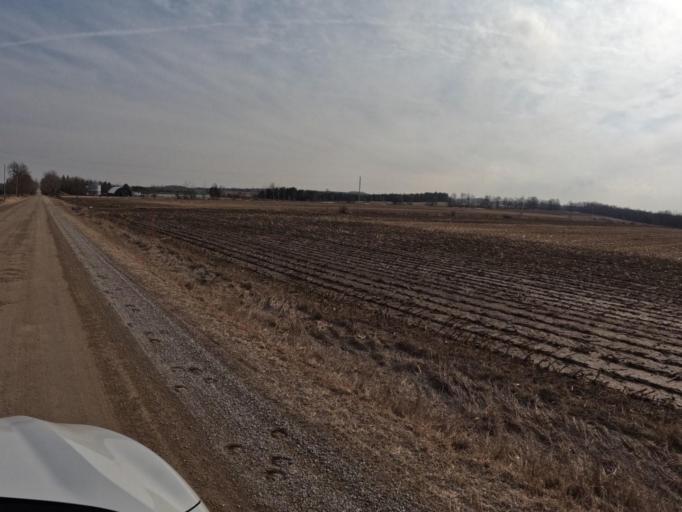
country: CA
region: Ontario
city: Orangeville
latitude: 43.9030
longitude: -80.2684
